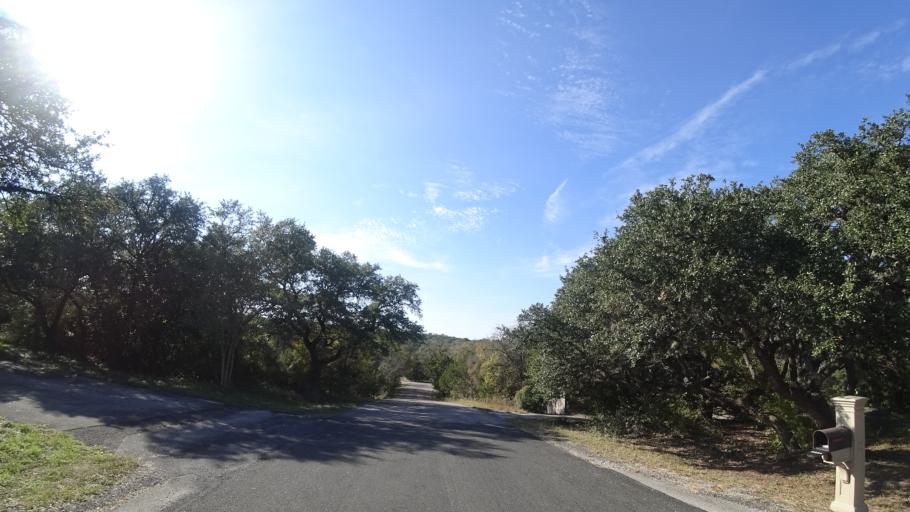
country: US
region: Texas
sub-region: Travis County
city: Bee Cave
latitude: 30.2328
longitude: -97.9354
